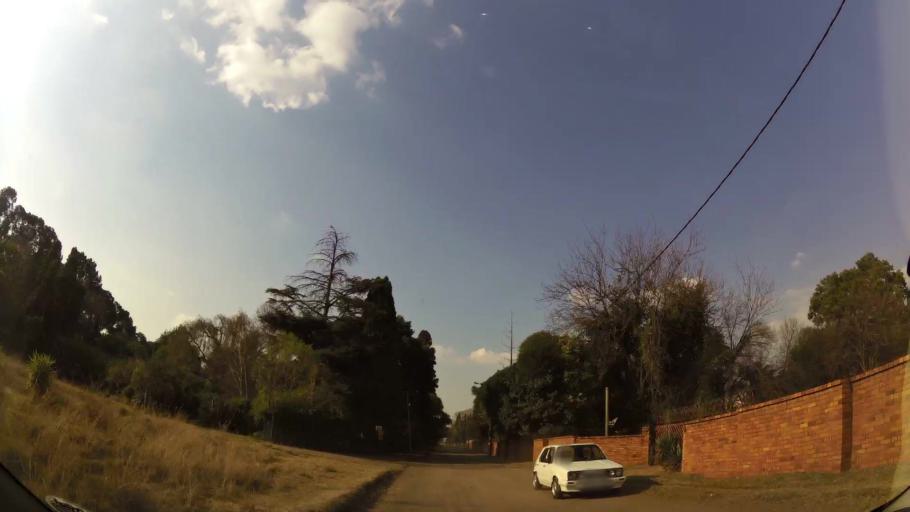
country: ZA
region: Gauteng
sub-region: Ekurhuleni Metropolitan Municipality
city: Benoni
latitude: -26.0993
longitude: 28.2925
